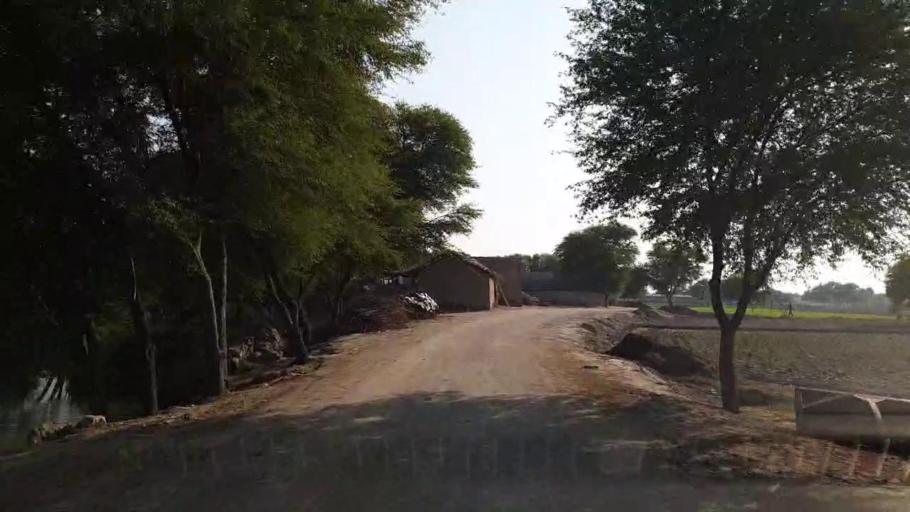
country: PK
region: Sindh
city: Sehwan
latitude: 26.4359
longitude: 67.7930
